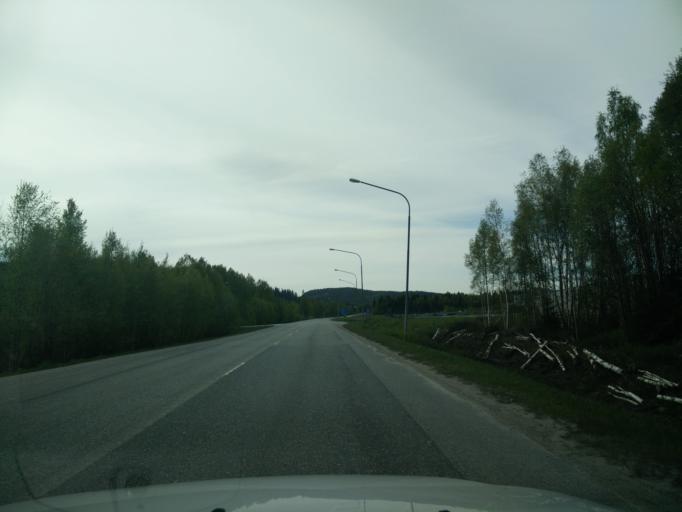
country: SE
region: Vaesternorrland
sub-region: OErnskoeldsviks Kommun
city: Bjasta
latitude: 63.2010
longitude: 18.4942
